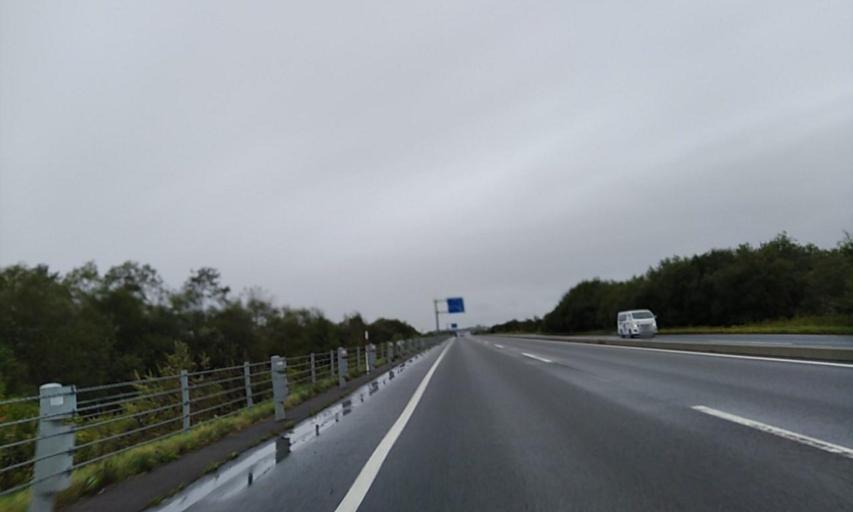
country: JP
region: Hokkaido
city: Kushiro
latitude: 43.0274
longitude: 144.2939
